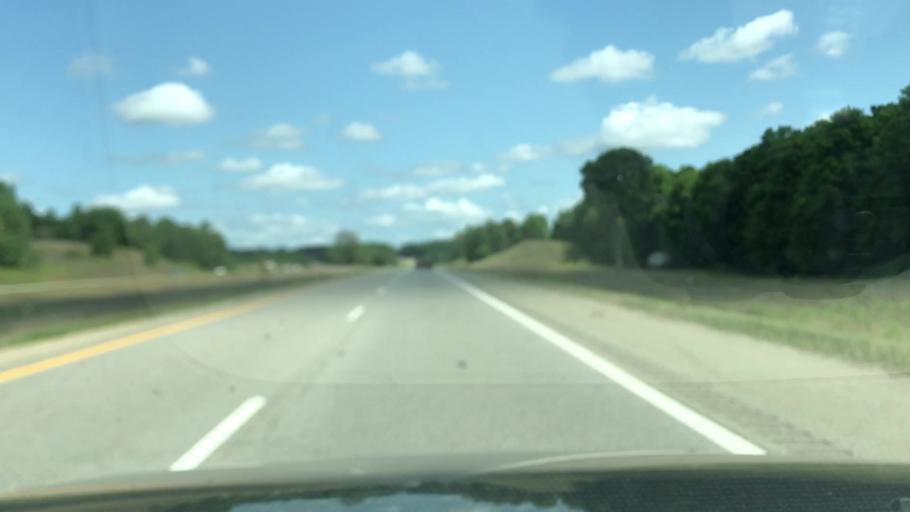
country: US
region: Michigan
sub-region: Osceola County
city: Reed City
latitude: 43.7942
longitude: -85.5337
